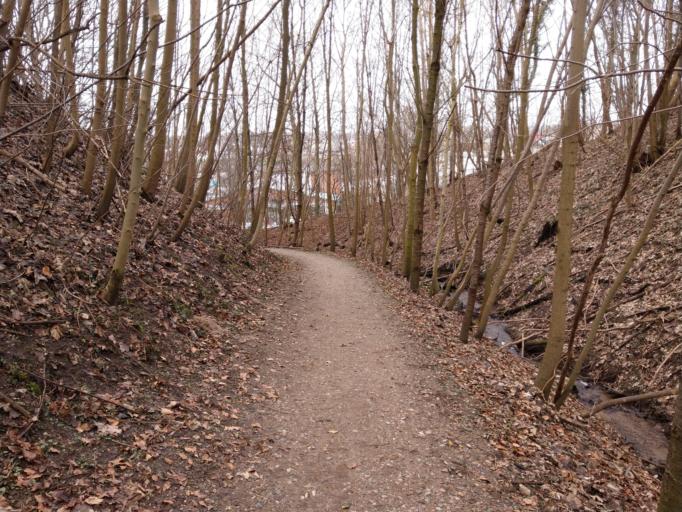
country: DE
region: Schleswig-Holstein
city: Flensburg
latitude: 54.8016
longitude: 9.4444
